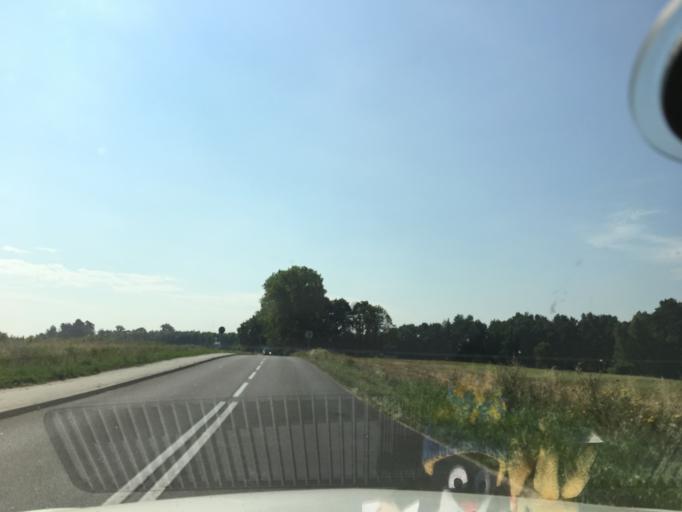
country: PL
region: West Pomeranian Voivodeship
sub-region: Powiat gryficki
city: Pobierowo
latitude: 54.0355
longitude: 14.8731
